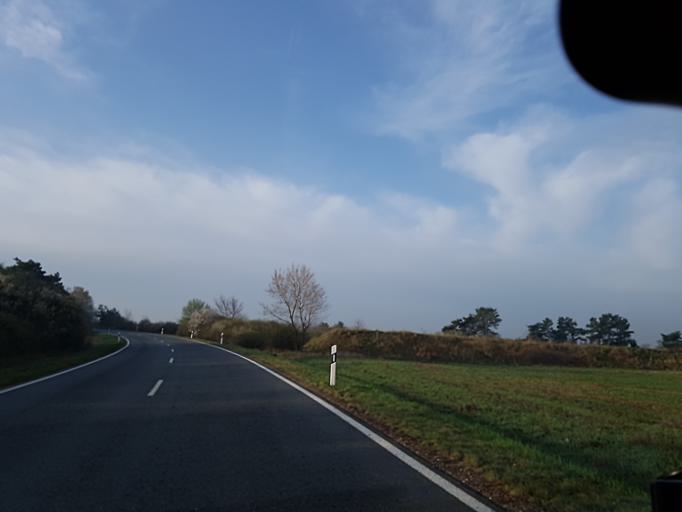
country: DE
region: Saxony
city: Strehla
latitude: 51.3714
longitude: 13.2657
